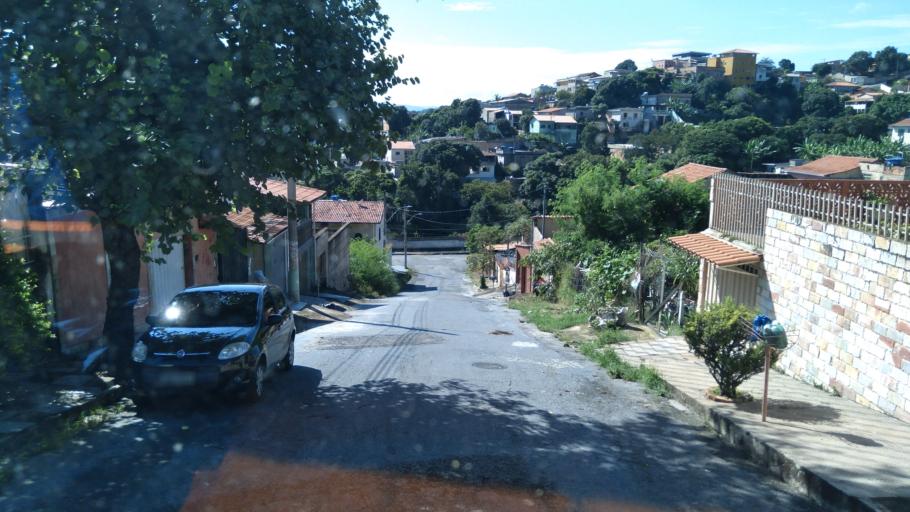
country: BR
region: Minas Gerais
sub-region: Santa Luzia
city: Santa Luzia
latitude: -19.8264
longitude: -43.8996
